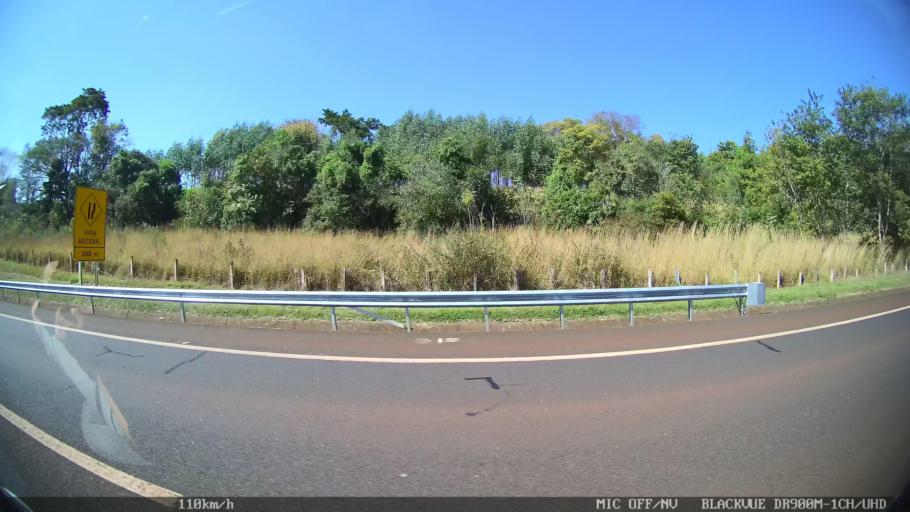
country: BR
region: Sao Paulo
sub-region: Franca
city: Franca
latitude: -20.6199
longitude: -47.4589
